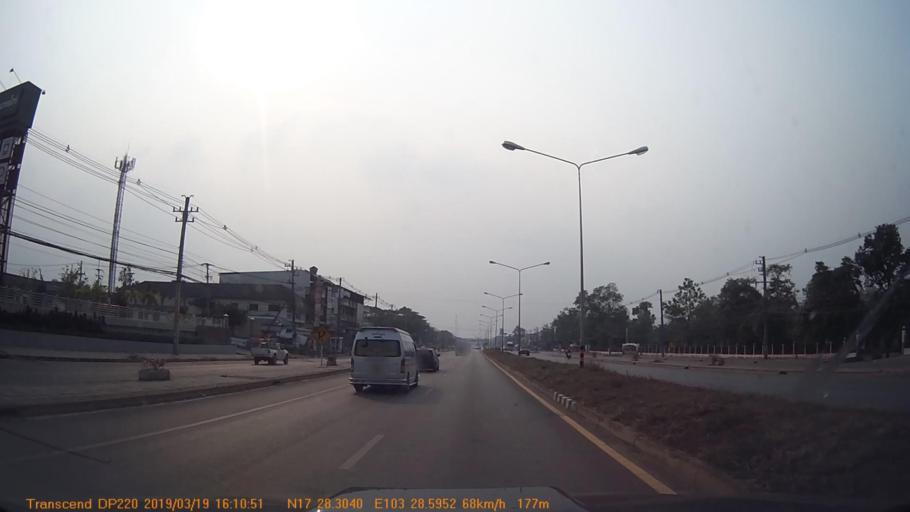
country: TH
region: Sakon Nakhon
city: Sawang Daen Din
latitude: 17.4719
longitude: 103.4760
